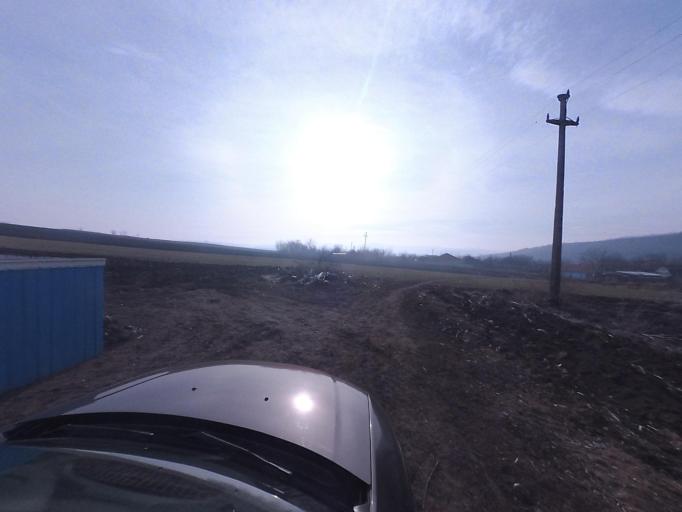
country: RO
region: Vaslui
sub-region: Comuna Solesti
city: Solesti
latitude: 46.8103
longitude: 27.7797
